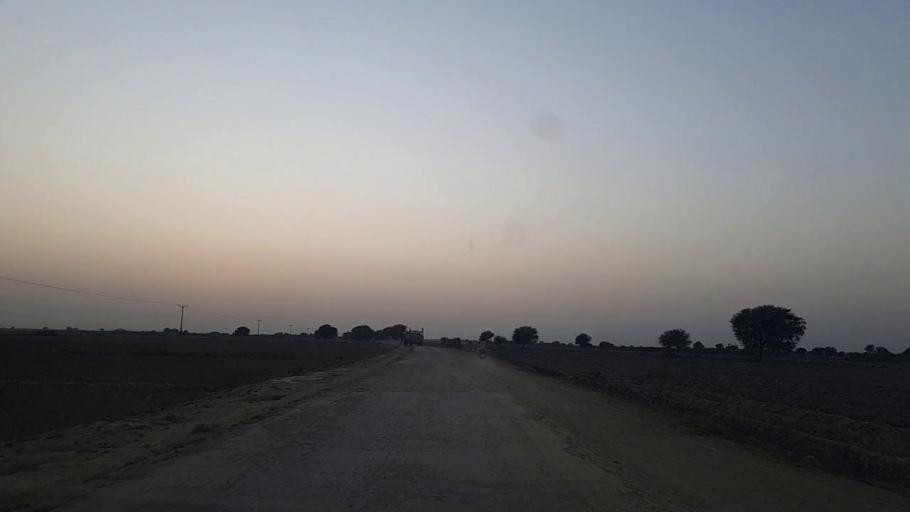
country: PK
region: Sindh
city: Naukot
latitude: 24.7526
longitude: 69.2988
